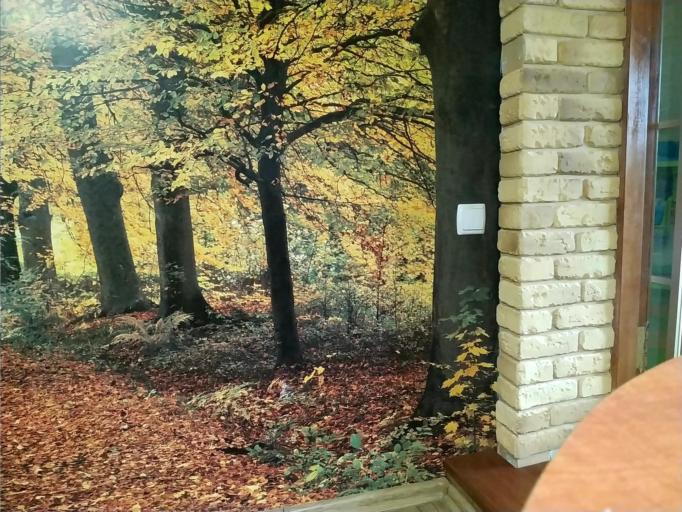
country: RU
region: Smolensk
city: Verkhnedneprovskiy
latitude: 54.9888
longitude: 33.2741
